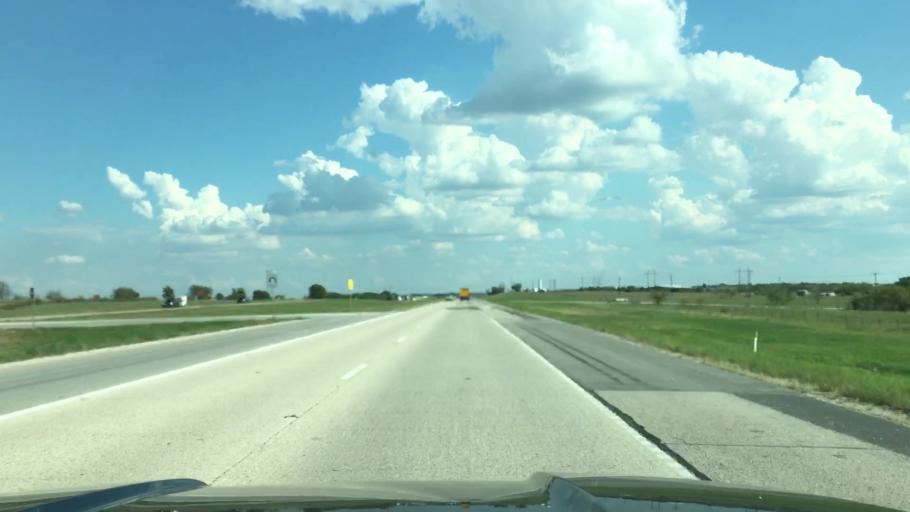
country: US
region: Texas
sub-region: Wise County
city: Decatur
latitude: 33.1875
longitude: -97.5544
